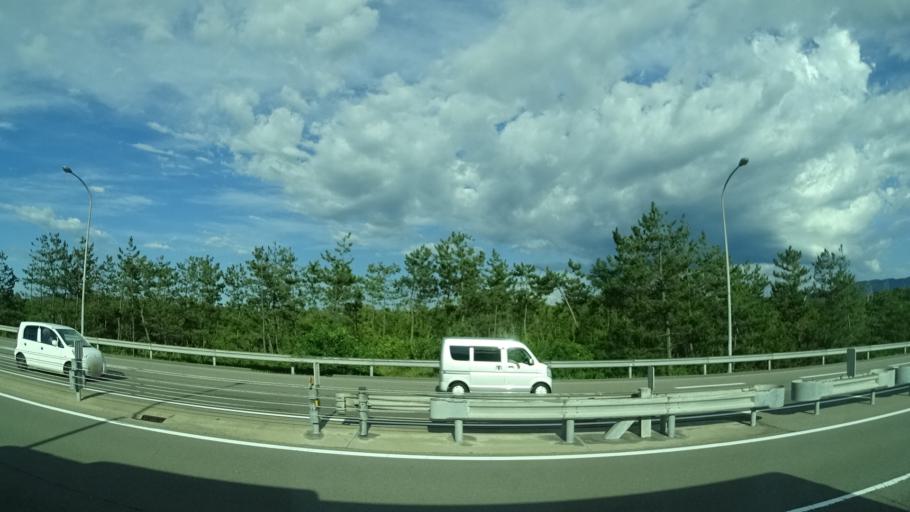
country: JP
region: Ishikawa
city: Hakui
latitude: 36.8607
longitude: 136.7580
